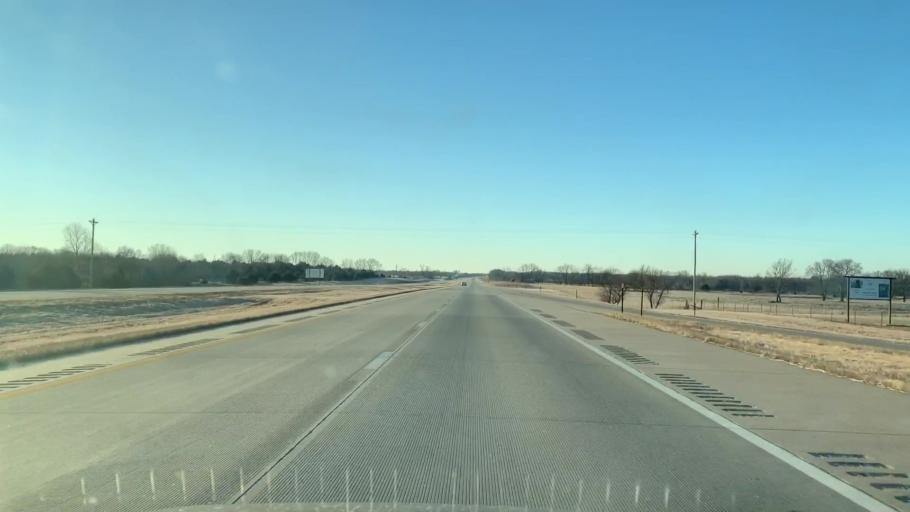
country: US
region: Kansas
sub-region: Linn County
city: Pleasanton
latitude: 38.0636
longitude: -94.7104
